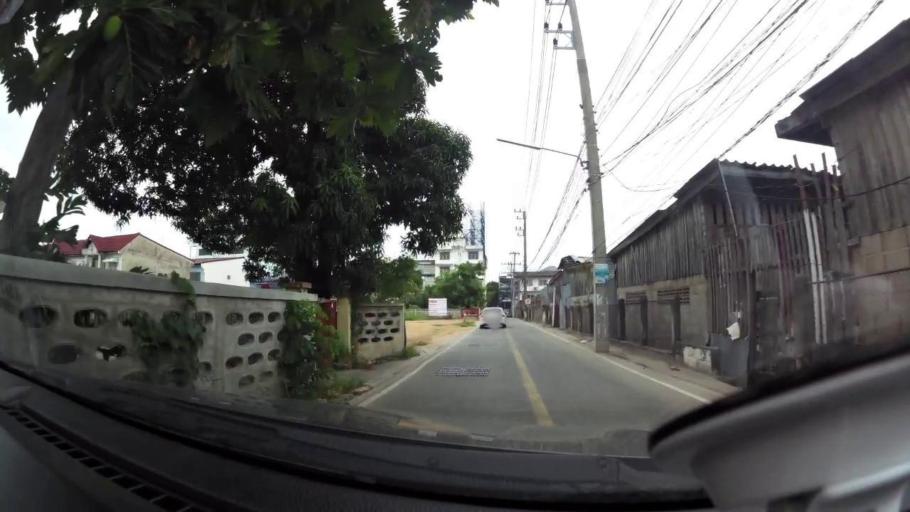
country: TH
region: Prachuap Khiri Khan
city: Hua Hin
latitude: 12.5835
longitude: 99.9508
